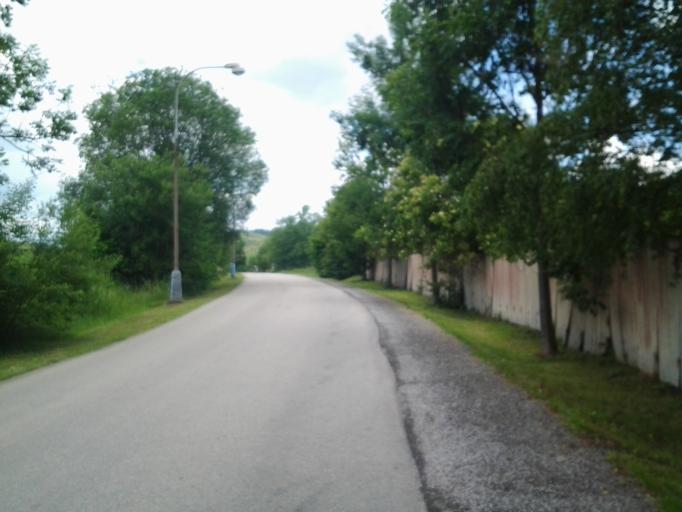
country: CZ
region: Jihocesky
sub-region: Okres Cesky Krumlov
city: Cesky Krumlov
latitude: 48.8277
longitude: 14.3066
